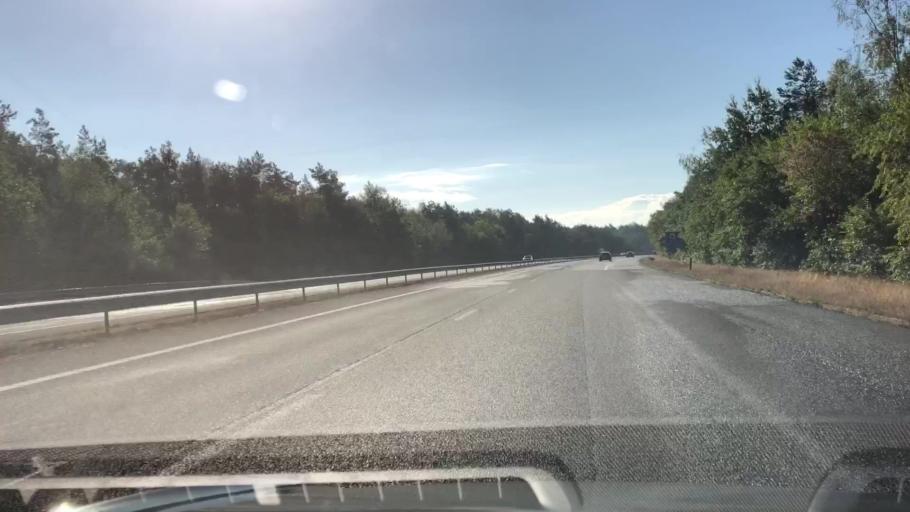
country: NL
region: Gelderland
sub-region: Gemeente Apeldoorn
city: Uddel
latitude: 52.2018
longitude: 5.8246
